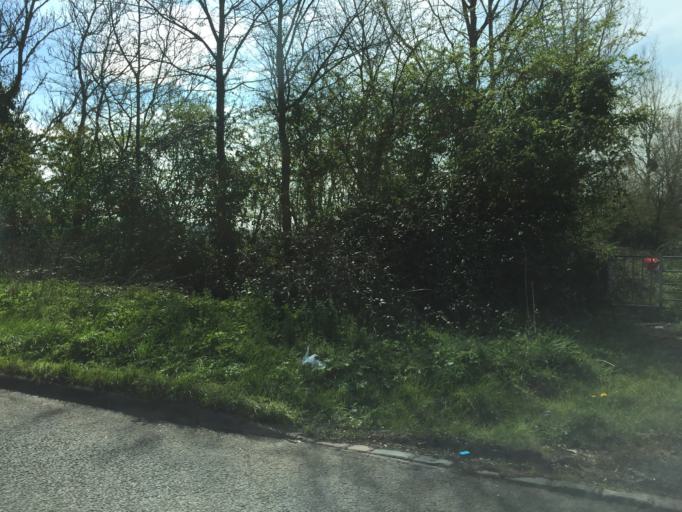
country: GB
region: England
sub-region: South Gloucestershire
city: Severn Beach
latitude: 51.5474
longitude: -2.6282
